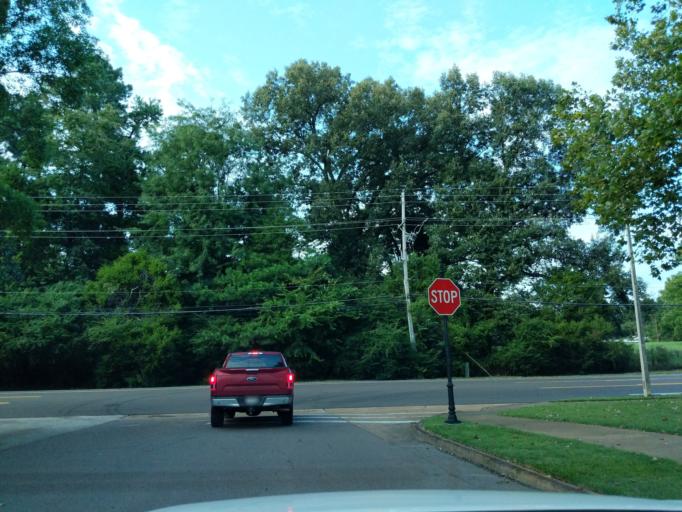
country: US
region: Tennessee
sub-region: Shelby County
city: Germantown
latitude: 35.0729
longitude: -89.7869
